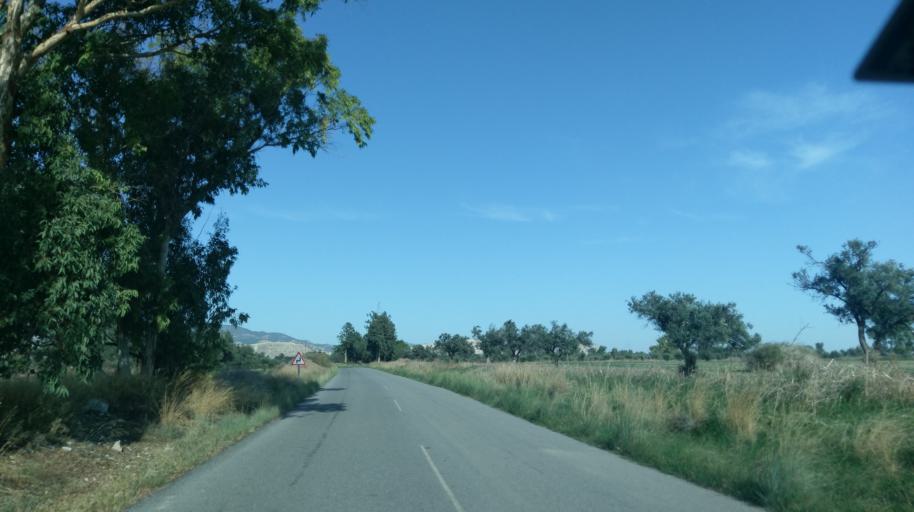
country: CY
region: Ammochostos
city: Lefkonoiko
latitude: 35.2968
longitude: 33.7404
